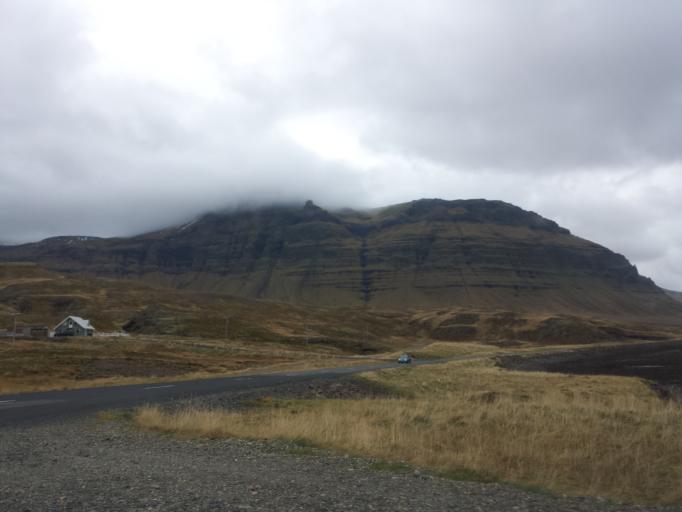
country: IS
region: West
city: Olafsvik
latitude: 64.9220
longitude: -23.2850
